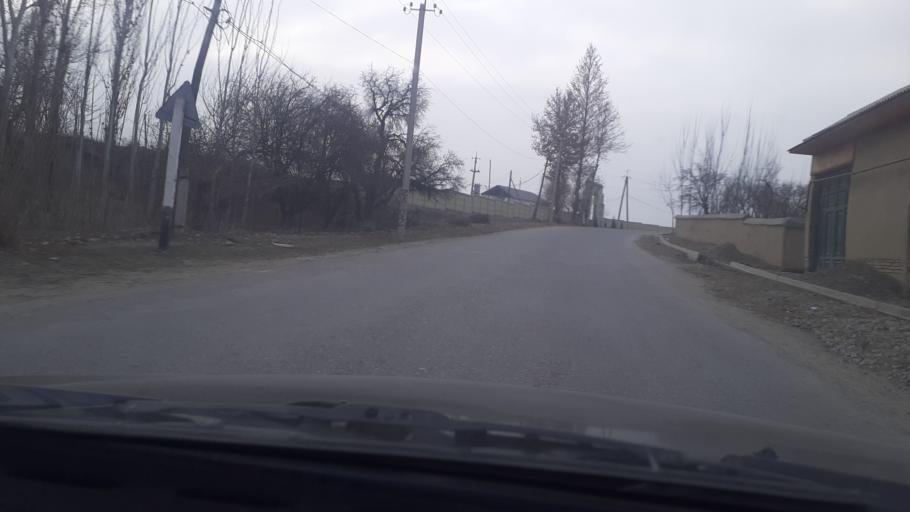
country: UZ
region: Namangan
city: Yangiqo`rg`on
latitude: 41.2047
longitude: 71.7053
